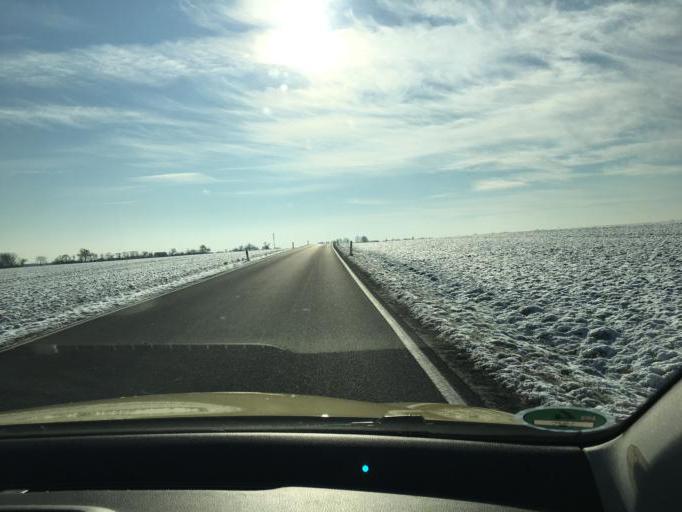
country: DE
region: Saxony
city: Belgershain
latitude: 51.2485
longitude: 12.5444
